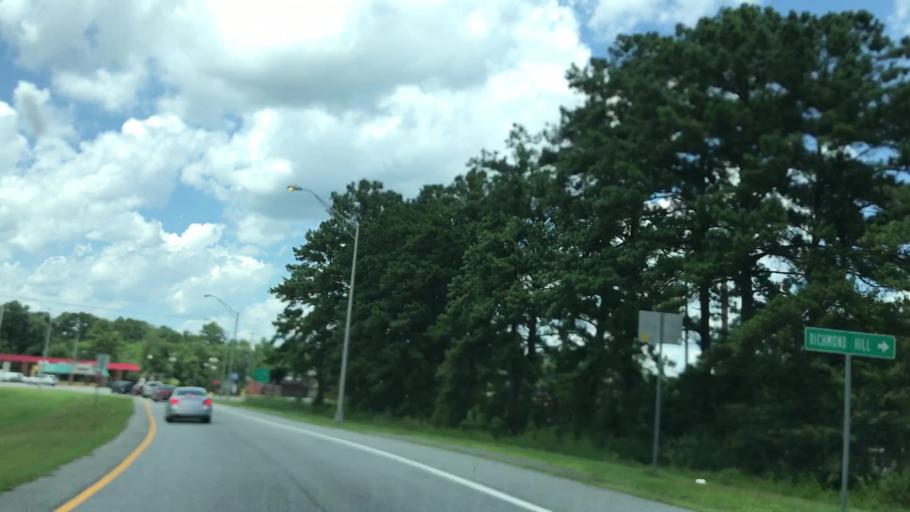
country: US
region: Georgia
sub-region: Bryan County
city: Richmond Hill
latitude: 31.9276
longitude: -81.3291
